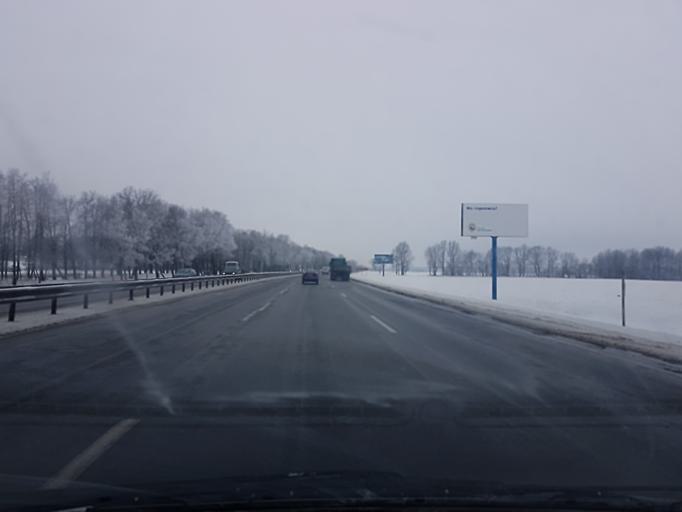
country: BY
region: Minsk
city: Shchomyslitsa
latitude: 53.8327
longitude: 27.4588
